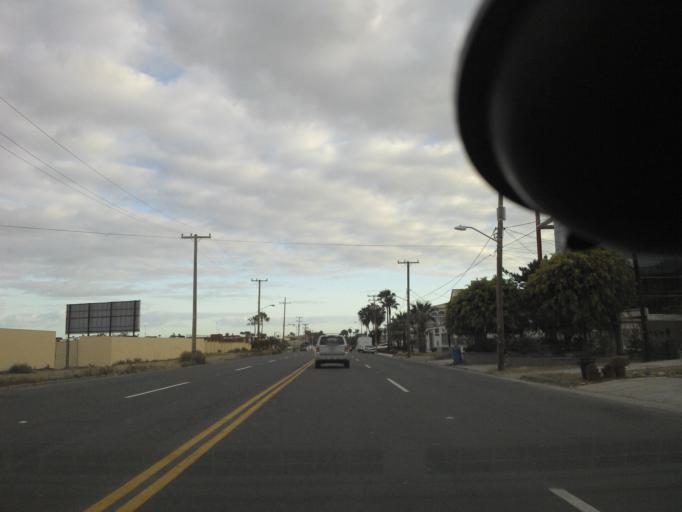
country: MX
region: Baja California
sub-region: Tijuana
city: La Esperanza [Granjas Familiares]
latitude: 32.5166
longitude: -117.1200
